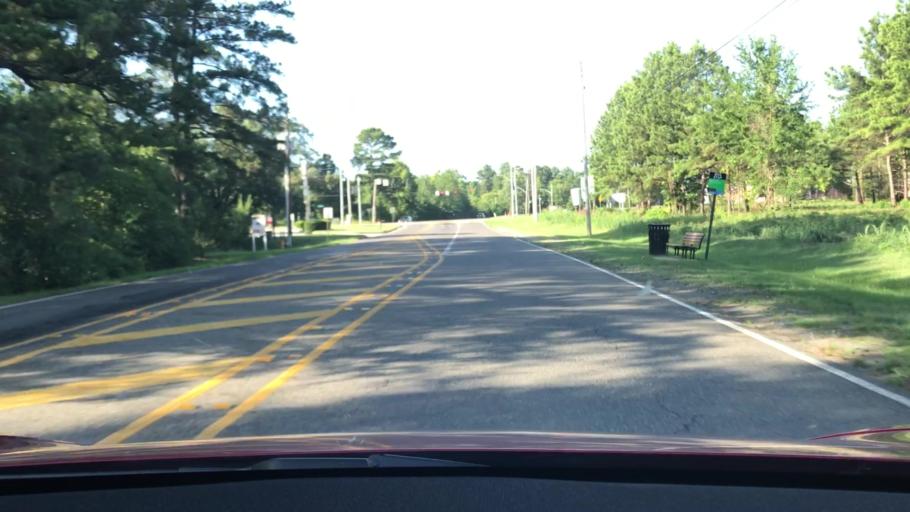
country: US
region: Louisiana
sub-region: Caddo Parish
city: Shreveport
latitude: 32.4435
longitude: -93.8444
